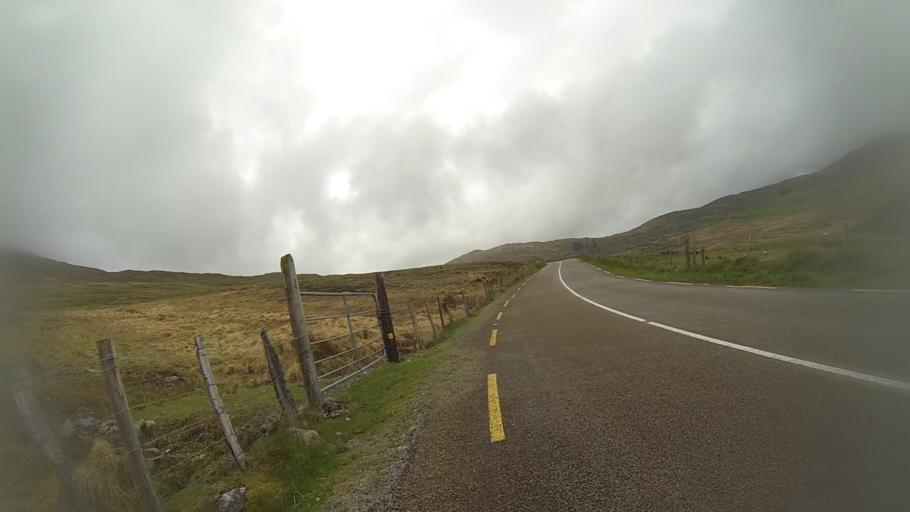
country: IE
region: Munster
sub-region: Ciarrai
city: Kenmare
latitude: 51.8781
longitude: -9.8020
